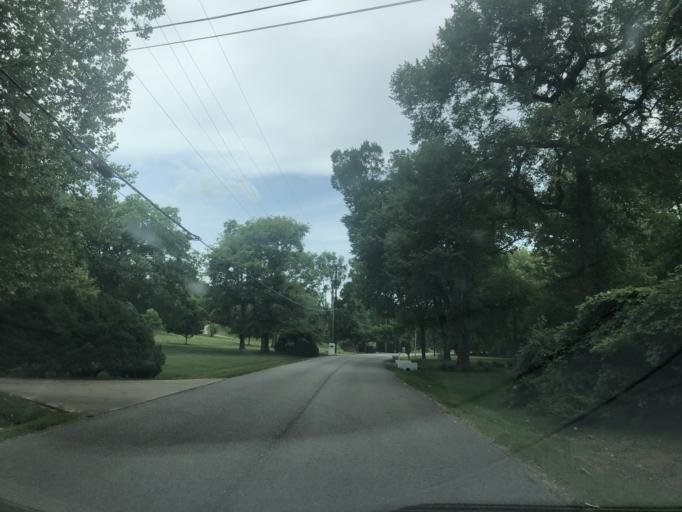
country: US
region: Tennessee
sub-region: Davidson County
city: Oak Hill
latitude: 36.0992
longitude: -86.7770
